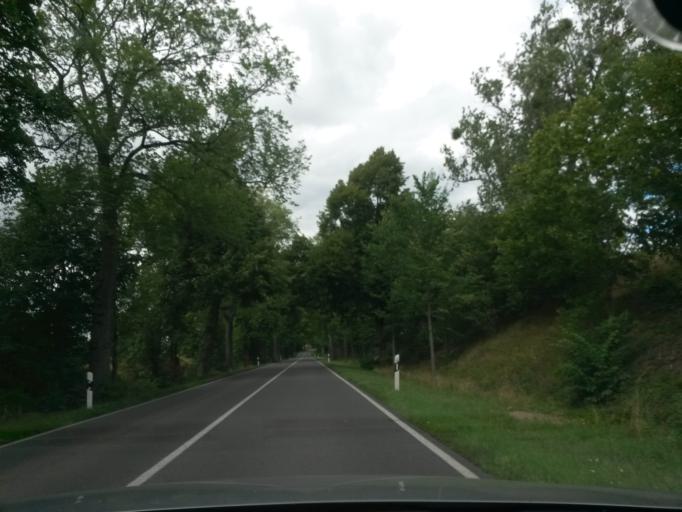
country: DE
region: Brandenburg
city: Angermunde
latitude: 52.9495
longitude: 13.9471
